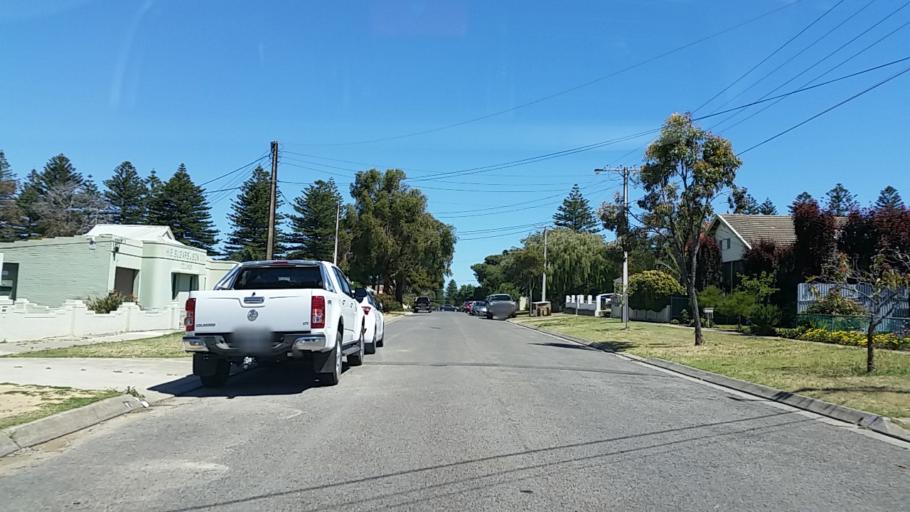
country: AU
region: South Australia
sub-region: Charles Sturt
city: Grange
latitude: -34.9008
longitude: 138.4936
